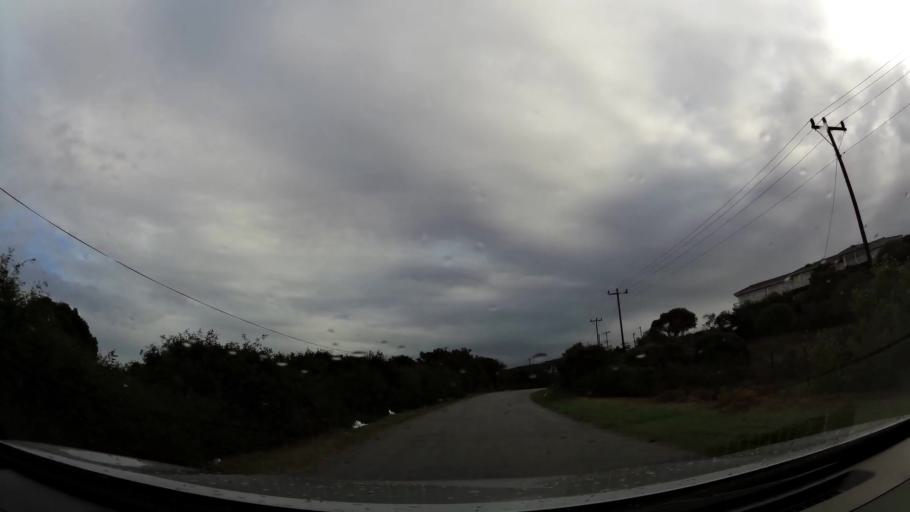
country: ZA
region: Eastern Cape
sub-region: Nelson Mandela Bay Metropolitan Municipality
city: Port Elizabeth
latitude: -34.0173
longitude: 25.4979
